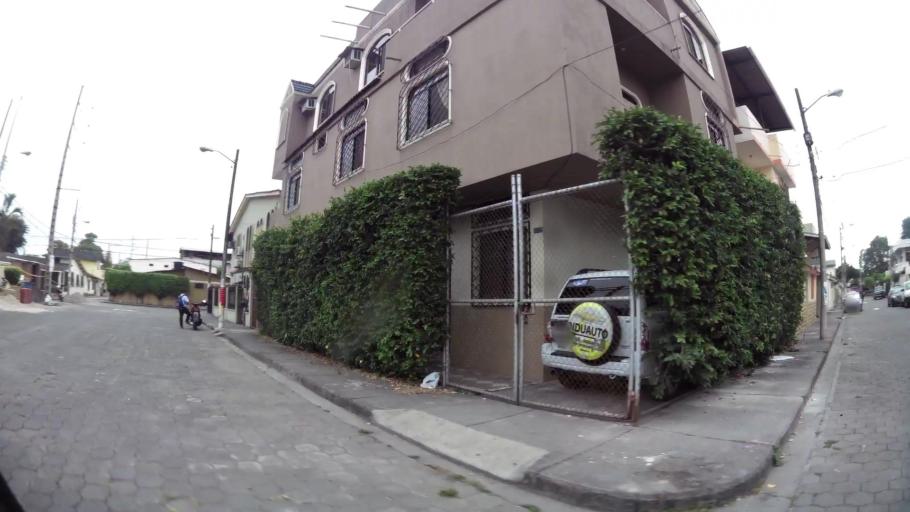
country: EC
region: Guayas
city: Eloy Alfaro
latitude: -2.1385
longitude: -79.9041
